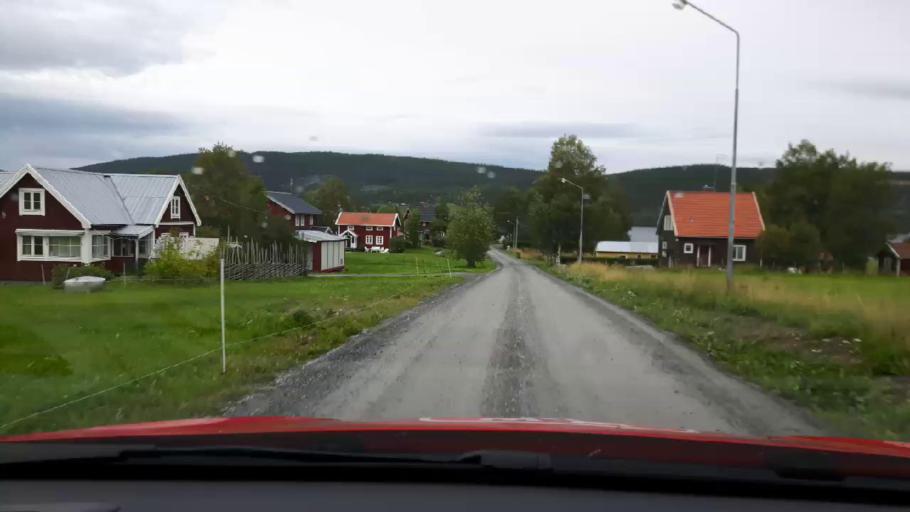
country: SE
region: Jaemtland
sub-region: Are Kommun
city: Are
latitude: 63.4918
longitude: 13.1213
